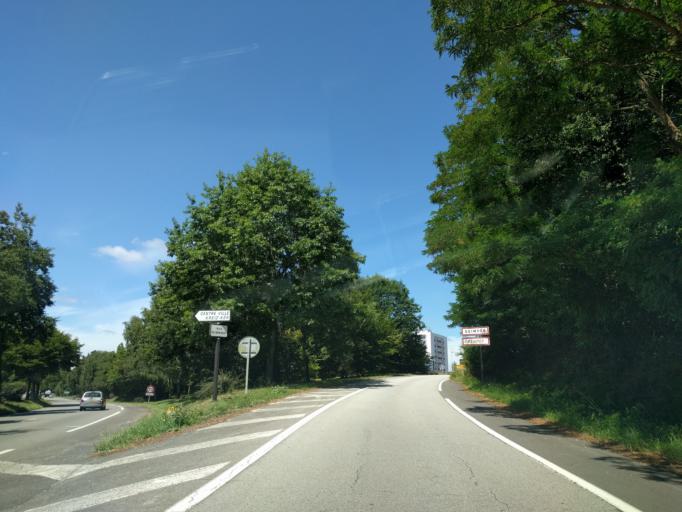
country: FR
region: Brittany
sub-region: Departement du Finistere
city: Quimper
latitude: 47.9804
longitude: -4.0999
